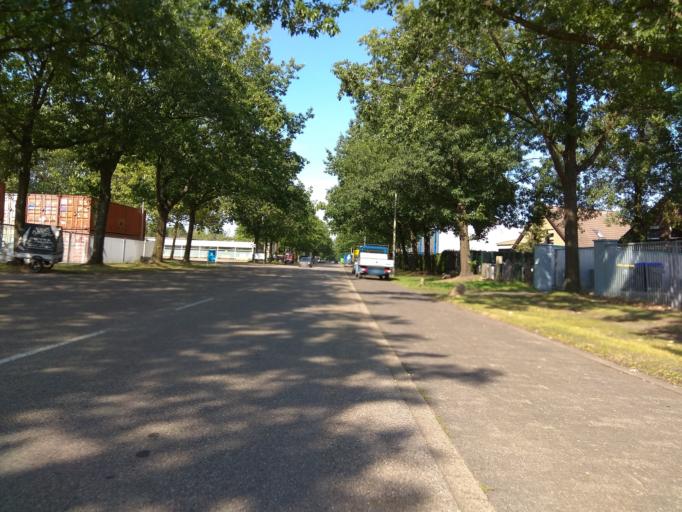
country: DE
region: North Rhine-Westphalia
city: Dorsten
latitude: 51.7132
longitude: 7.0031
